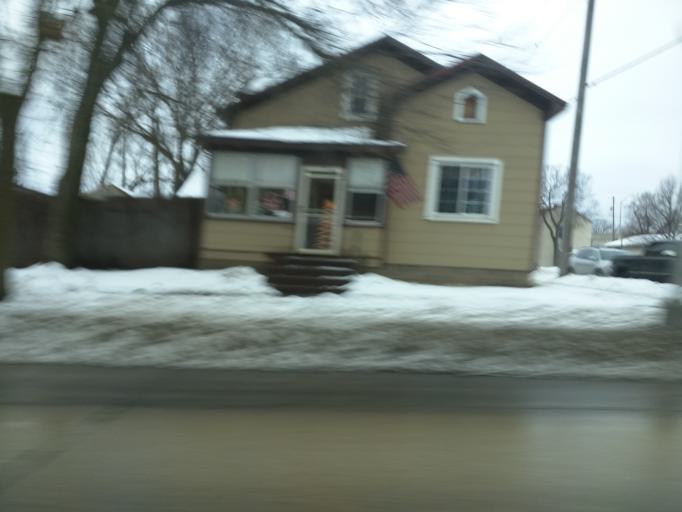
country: US
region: Wisconsin
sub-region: La Crosse County
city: North La Crosse
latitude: 43.8311
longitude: -91.2481
